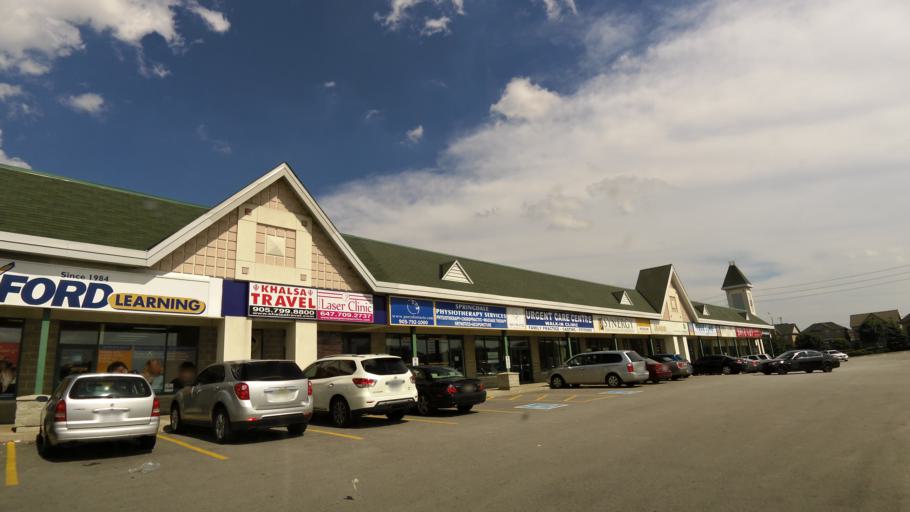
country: CA
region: Ontario
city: Brampton
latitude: 43.7606
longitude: -79.7283
